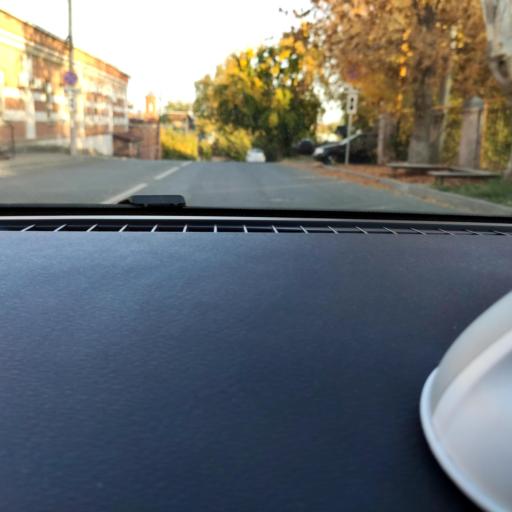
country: RU
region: Samara
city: Samara
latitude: 53.1804
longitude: 50.0965
